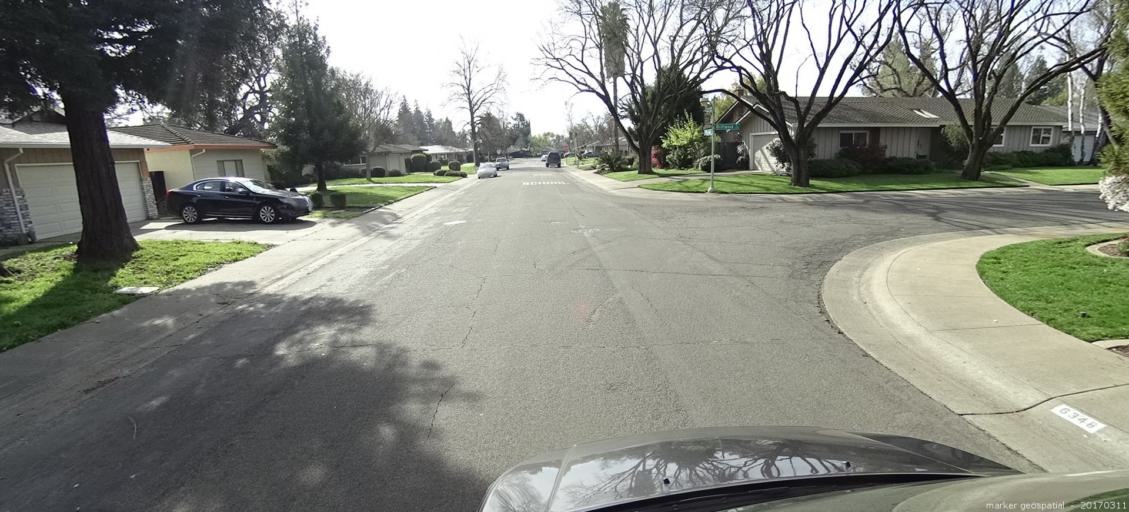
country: US
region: California
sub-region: Yolo County
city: West Sacramento
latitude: 38.5110
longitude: -121.5492
